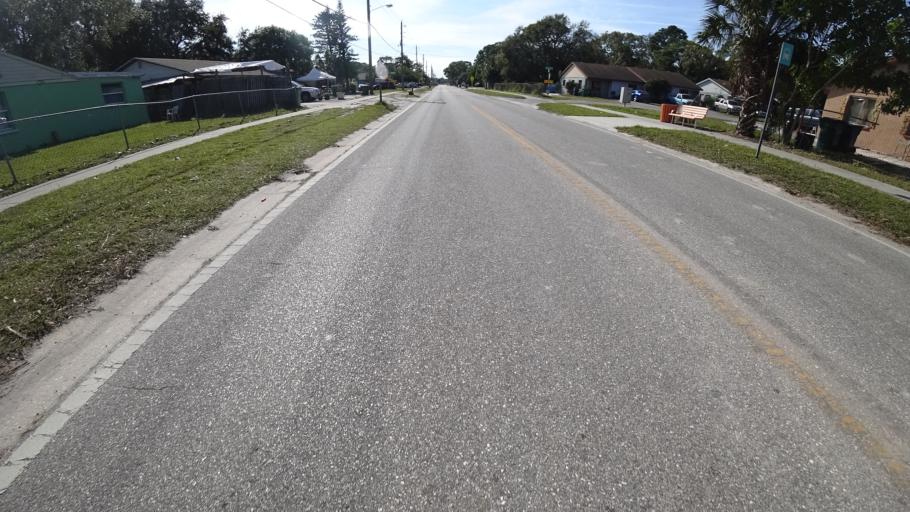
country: US
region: Florida
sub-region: Manatee County
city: Whitfield
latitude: 27.4347
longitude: -82.5590
